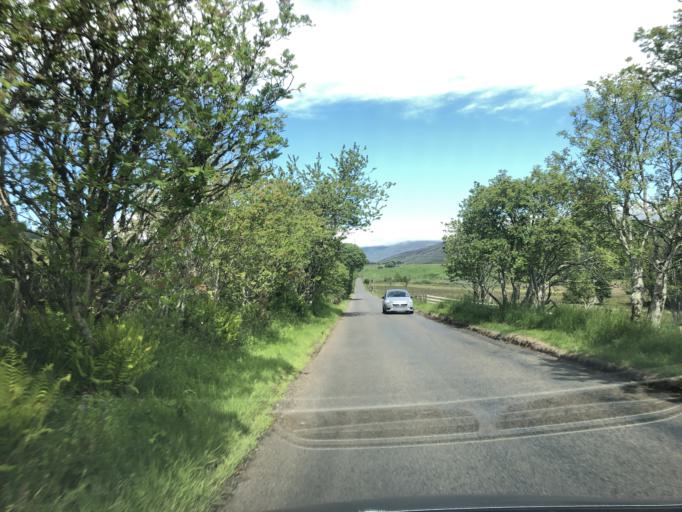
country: GB
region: Scotland
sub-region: Angus
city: Kirriemuir
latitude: 56.7479
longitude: -3.0136
